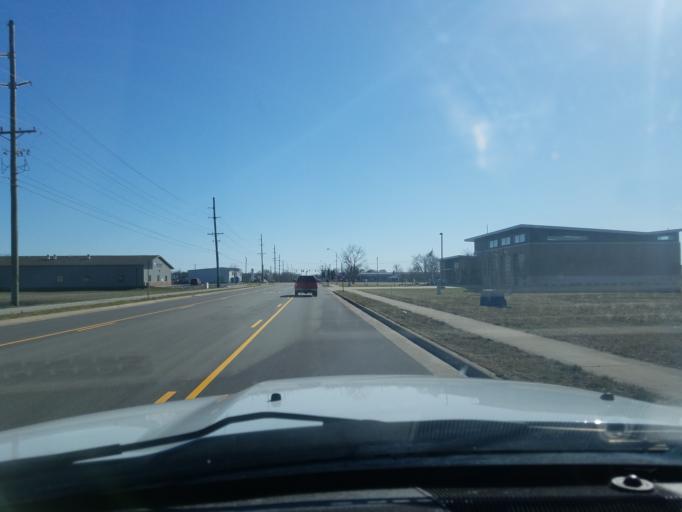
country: US
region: Indiana
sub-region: Shelby County
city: Shelbyville
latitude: 39.5185
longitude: -85.7427
